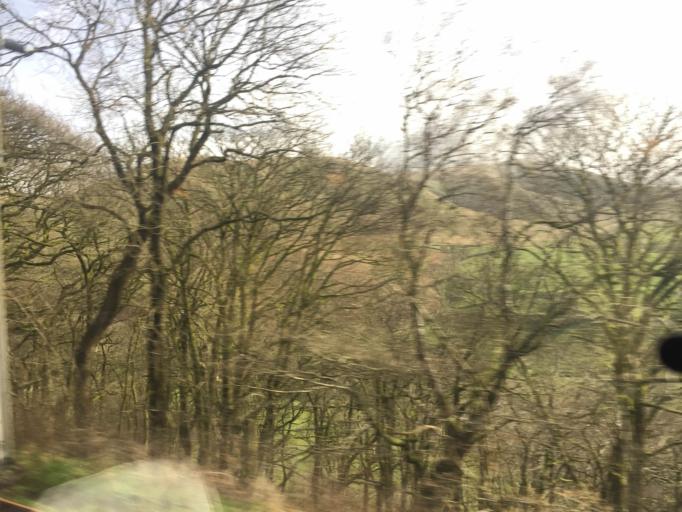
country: GB
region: England
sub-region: Cumbria
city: Sedbergh
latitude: 54.3752
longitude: -2.5823
